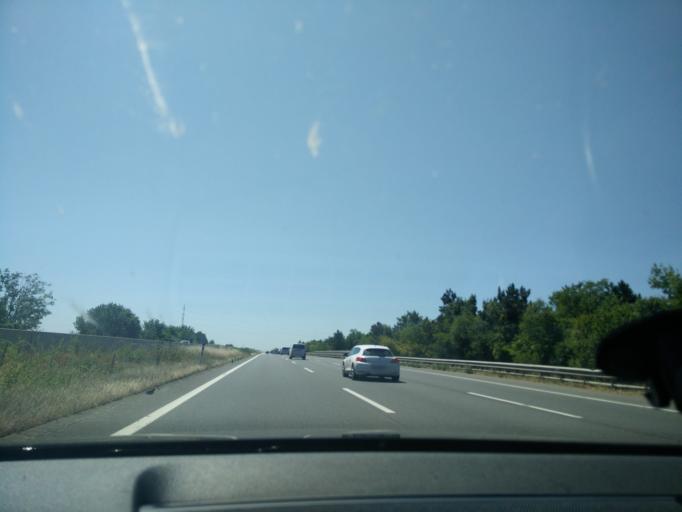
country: AT
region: Lower Austria
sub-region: Politischer Bezirk Baden
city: Leobersdorf
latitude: 47.9214
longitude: 16.2085
